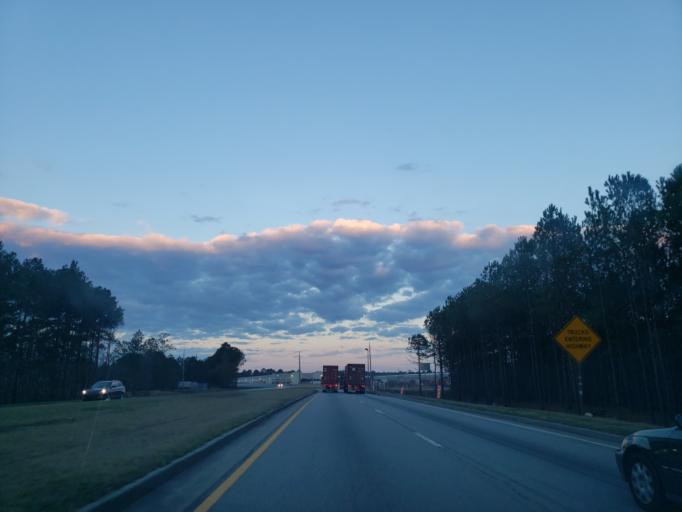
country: US
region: Georgia
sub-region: Chatham County
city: Port Wentworth
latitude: 32.1636
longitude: -81.1924
